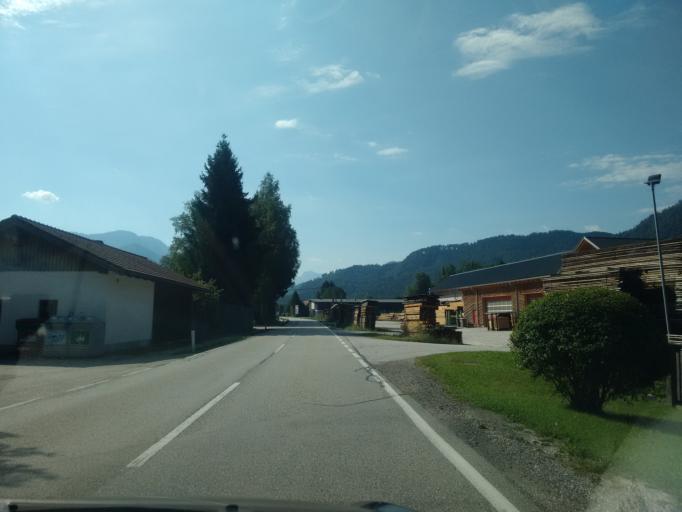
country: AT
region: Upper Austria
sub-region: Politischer Bezirk Gmunden
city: Gruenau im Almtal
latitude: 47.8706
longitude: 13.9442
